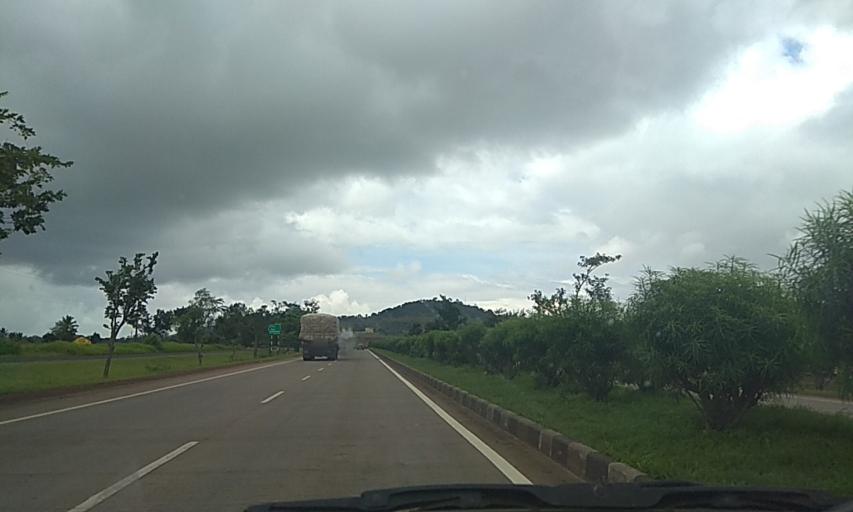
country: IN
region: Karnataka
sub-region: Belgaum
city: Sankeshwar
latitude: 16.2651
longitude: 74.4648
